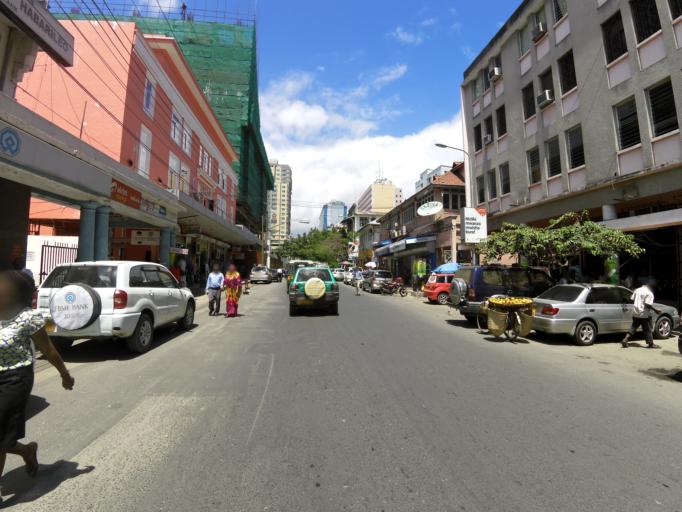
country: TZ
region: Dar es Salaam
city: Dar es Salaam
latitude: -6.8170
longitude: 39.2891
